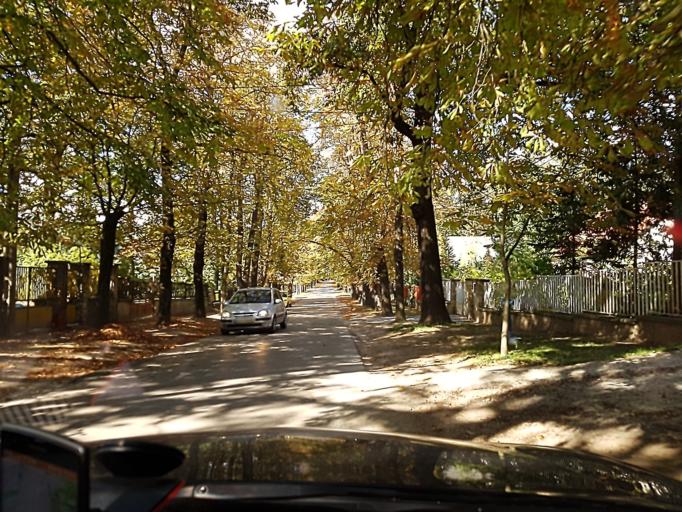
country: HU
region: Pest
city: Piliscsaba
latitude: 47.6393
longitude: 18.8339
